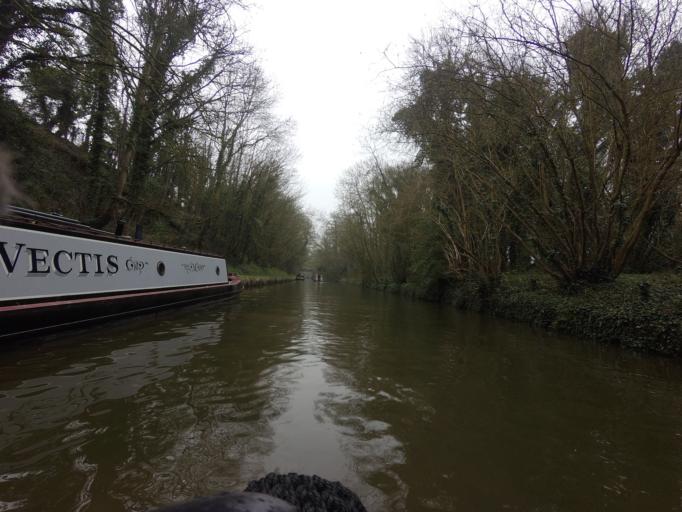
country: GB
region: England
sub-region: Hertfordshire
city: Tring
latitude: 51.8001
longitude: -0.6294
